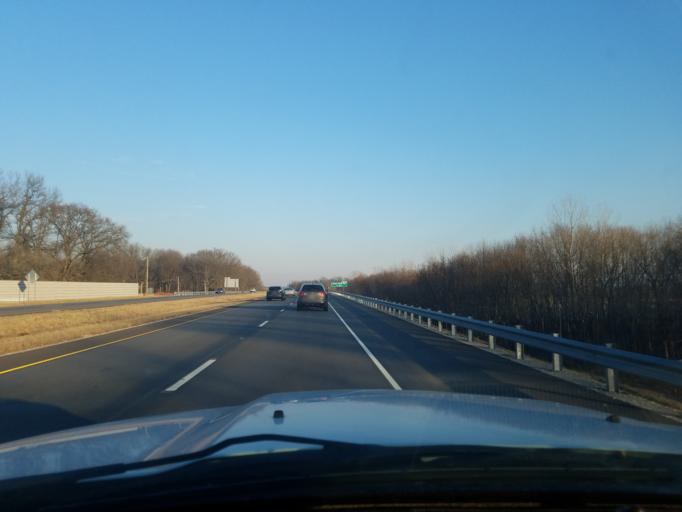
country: US
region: Indiana
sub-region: Vanderburgh County
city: Evansville
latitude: 37.9394
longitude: -87.5079
